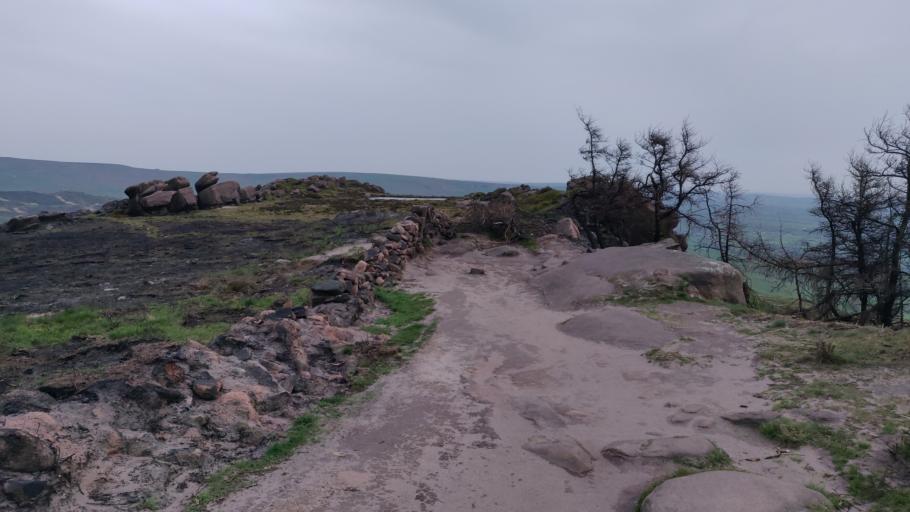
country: GB
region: England
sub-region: Staffordshire
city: Leek
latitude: 53.1638
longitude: -1.9969
